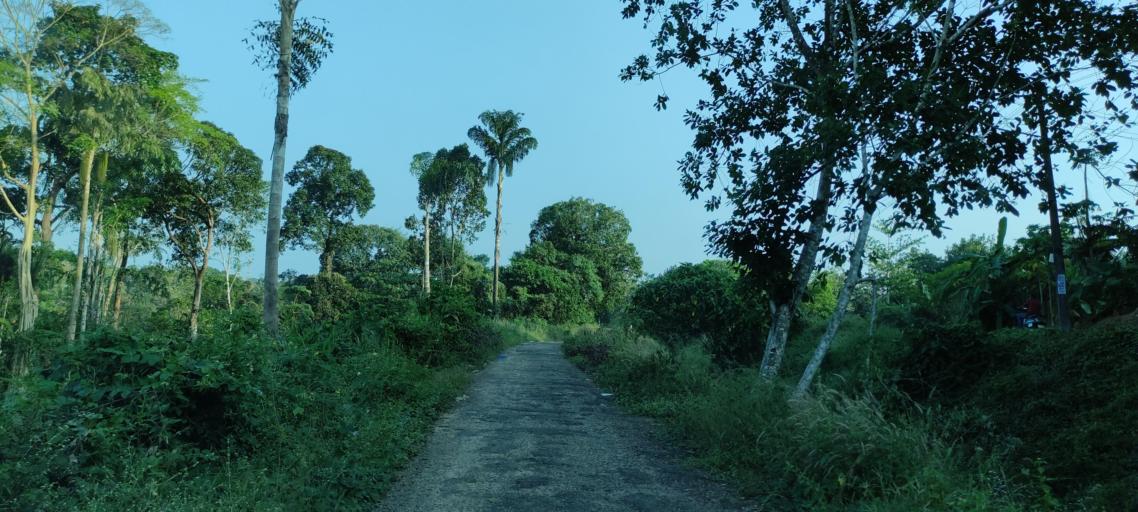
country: IN
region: Kerala
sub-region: Pattanamtitta
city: Adur
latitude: 9.1366
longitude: 76.7331
